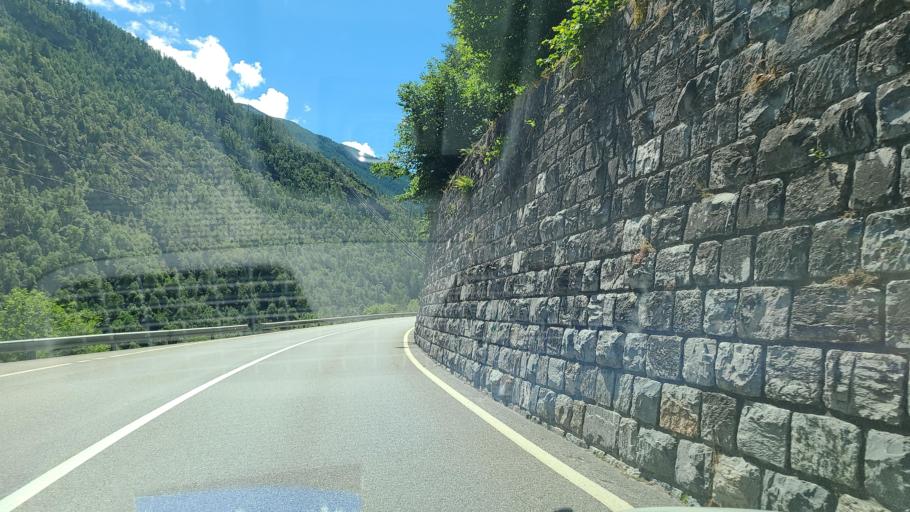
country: CH
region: Valais
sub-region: Visp District
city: Stalden
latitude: 46.2136
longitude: 7.8839
